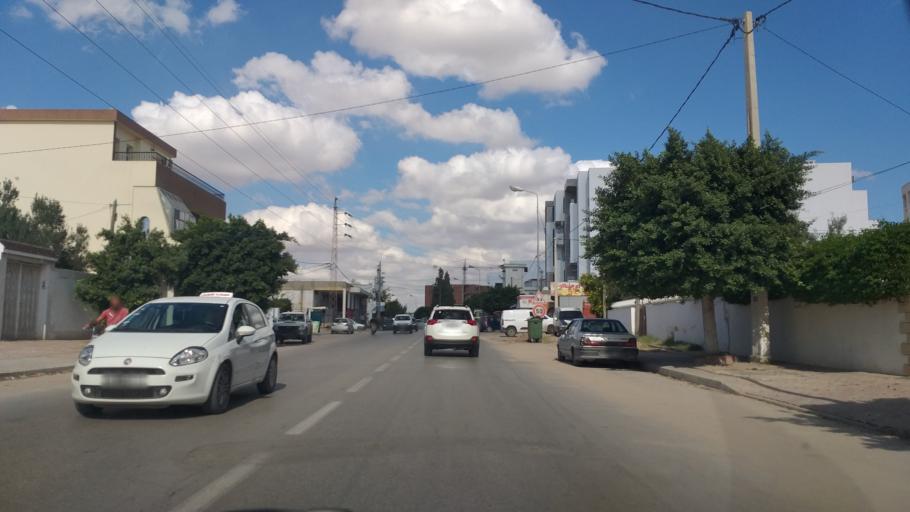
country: TN
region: Safaqis
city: Al Qarmadah
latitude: 34.7764
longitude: 10.7770
